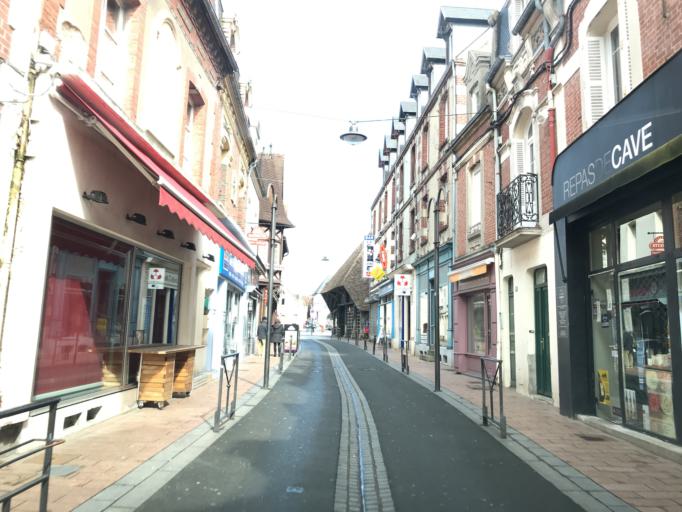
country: FR
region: Lower Normandy
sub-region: Departement du Calvados
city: Dives-sur-Mer
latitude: 49.2859
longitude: -0.0972
